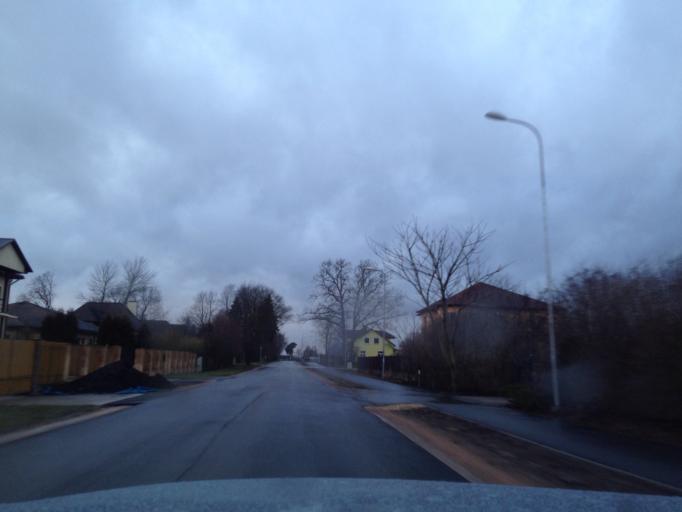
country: LV
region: Marupe
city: Marupe
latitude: 56.8911
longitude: 24.0314
